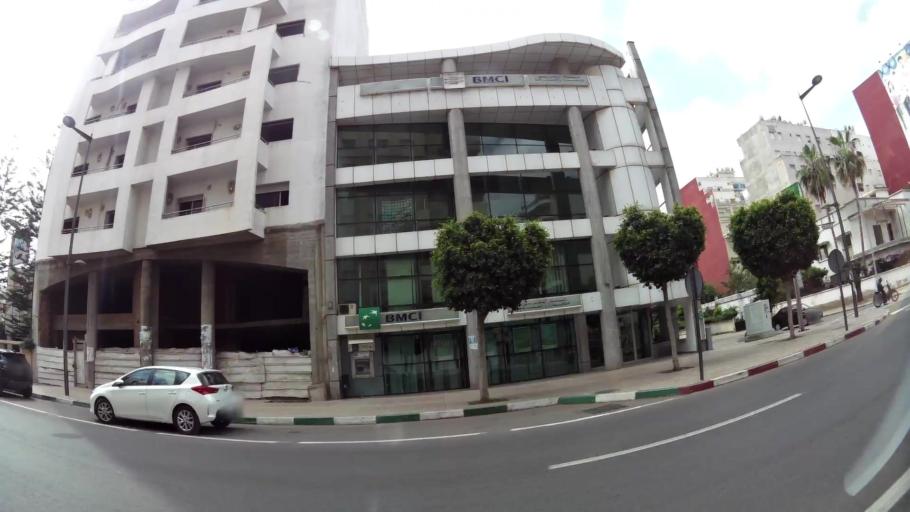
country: MA
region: Gharb-Chrarda-Beni Hssen
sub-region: Kenitra Province
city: Kenitra
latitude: 34.2566
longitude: -6.5921
